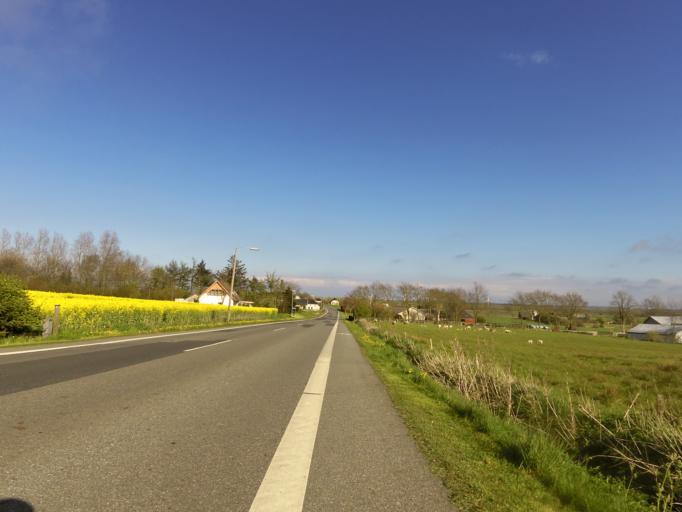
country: DK
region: South Denmark
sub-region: Tonder Kommune
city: Sherrebek
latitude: 55.1571
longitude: 8.8182
